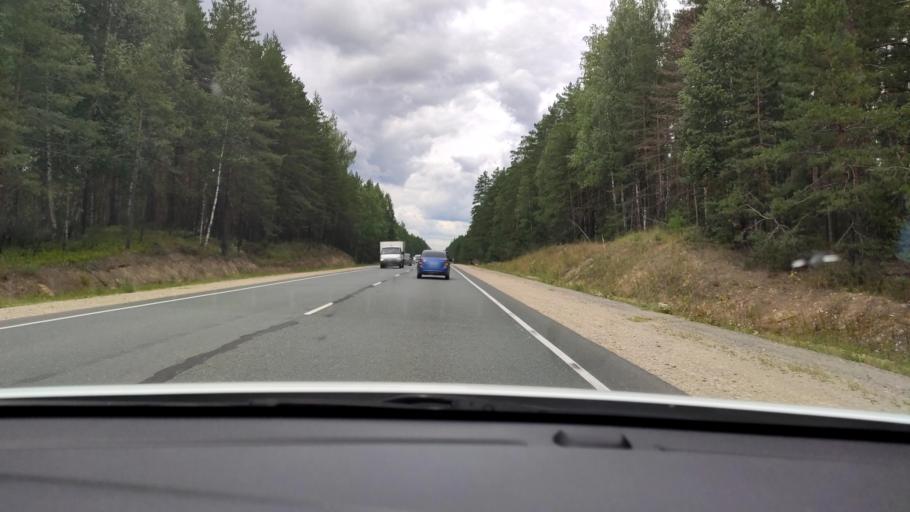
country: RU
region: Mariy-El
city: Pomary
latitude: 56.0413
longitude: 48.3782
